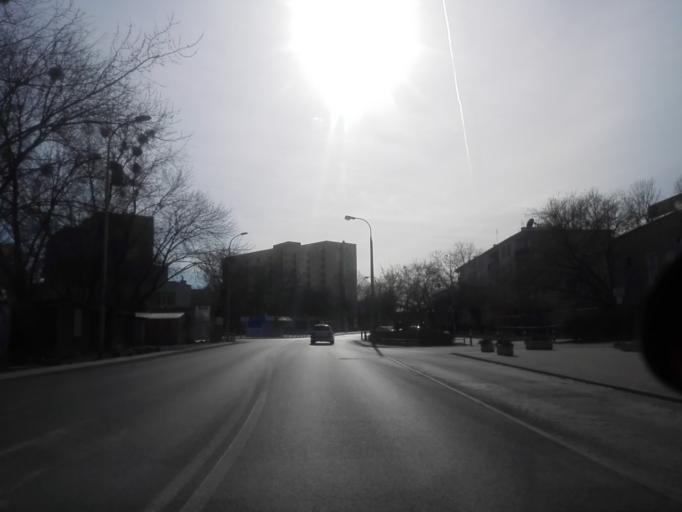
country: PL
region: Masovian Voivodeship
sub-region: Warszawa
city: Mokotow
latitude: 52.1713
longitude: 21.0046
